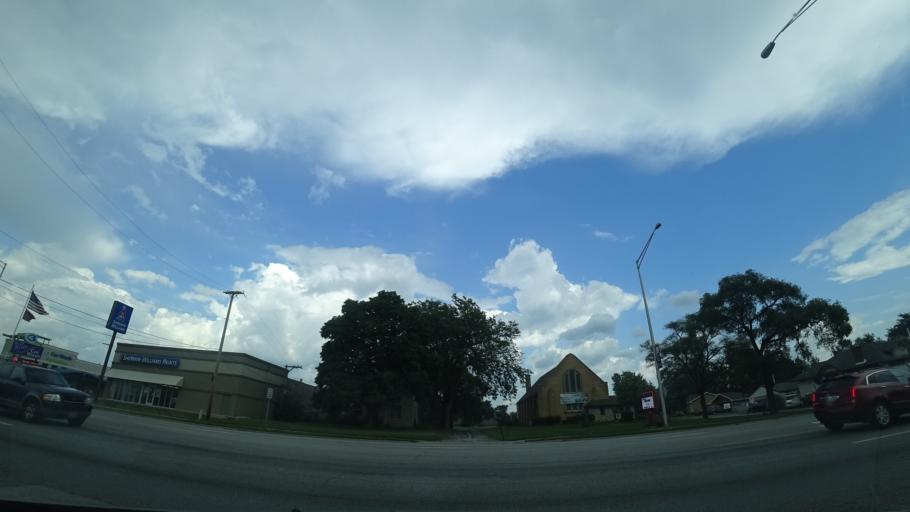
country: US
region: Illinois
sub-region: Cook County
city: Alsip
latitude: 41.6718
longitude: -87.7392
